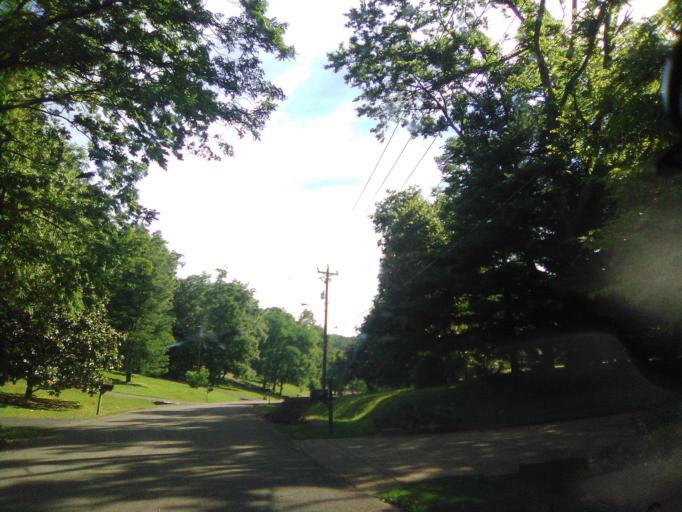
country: US
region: Tennessee
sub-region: Davidson County
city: Belle Meade
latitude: 36.1024
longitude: -86.9139
